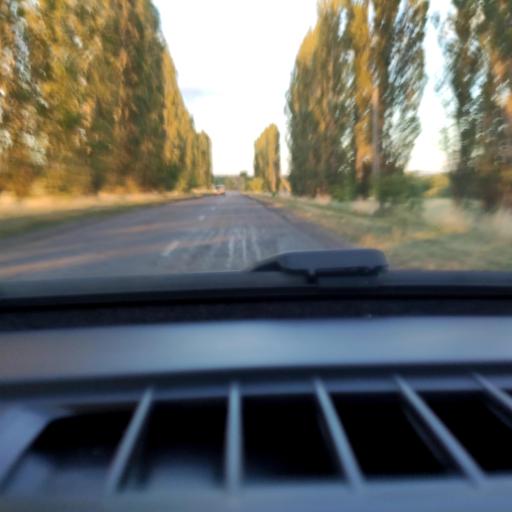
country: RU
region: Voronezj
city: Orlovo
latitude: 51.6159
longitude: 39.8017
